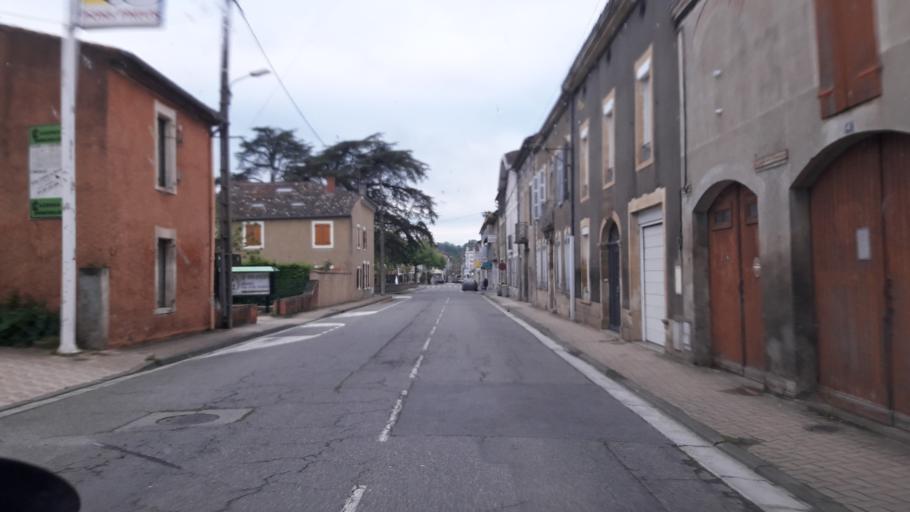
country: FR
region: Midi-Pyrenees
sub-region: Departement de la Haute-Garonne
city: Cazeres
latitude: 43.2093
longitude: 1.0857
